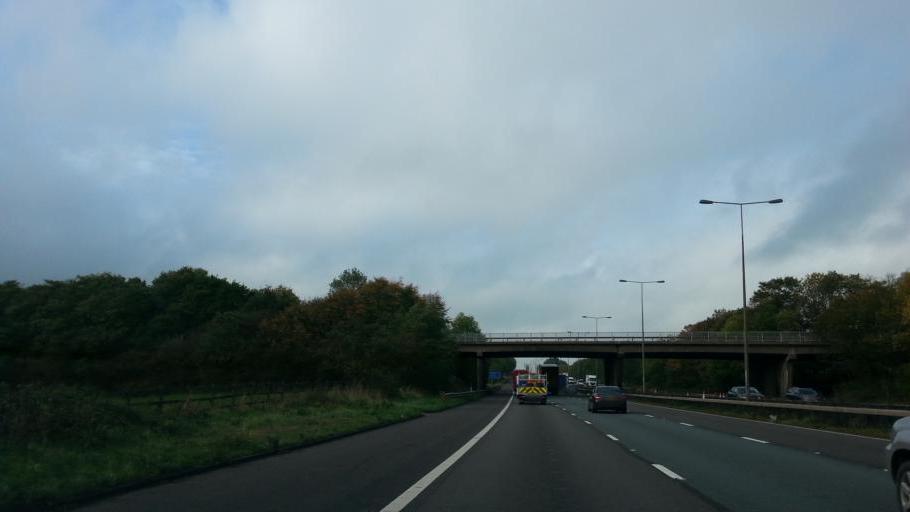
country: GB
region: England
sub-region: Staffordshire
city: Newcastle under Lyme
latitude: 52.9878
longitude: -2.2553
